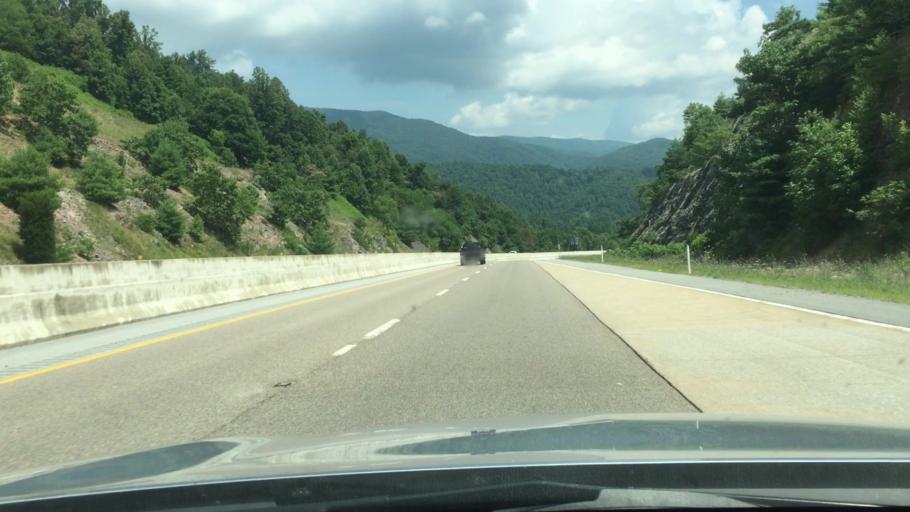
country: US
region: Tennessee
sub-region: Unicoi County
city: Banner Hill
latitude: 36.0558
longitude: -82.5128
